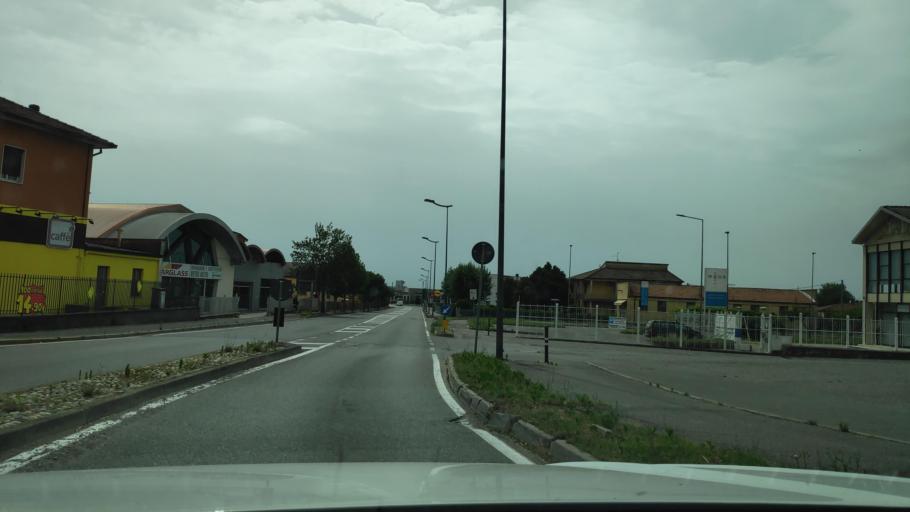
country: IT
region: Lombardy
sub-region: Provincia di Brescia
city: Orzinuovi
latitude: 45.4065
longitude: 9.9253
